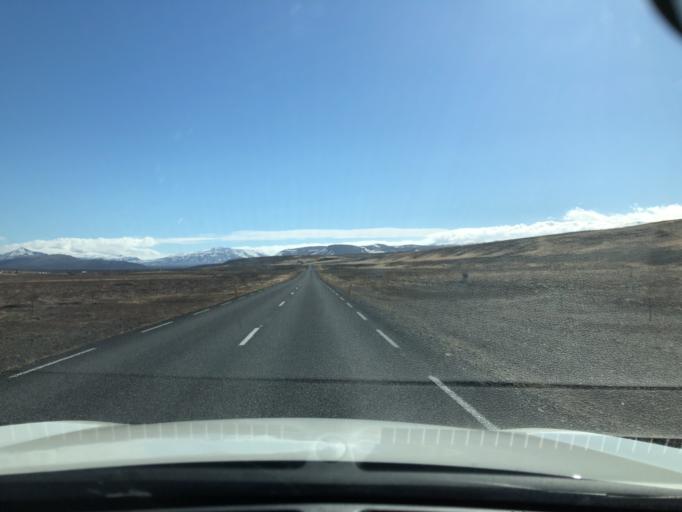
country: IS
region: South
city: Hveragerdi
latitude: 64.7005
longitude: -21.0872
